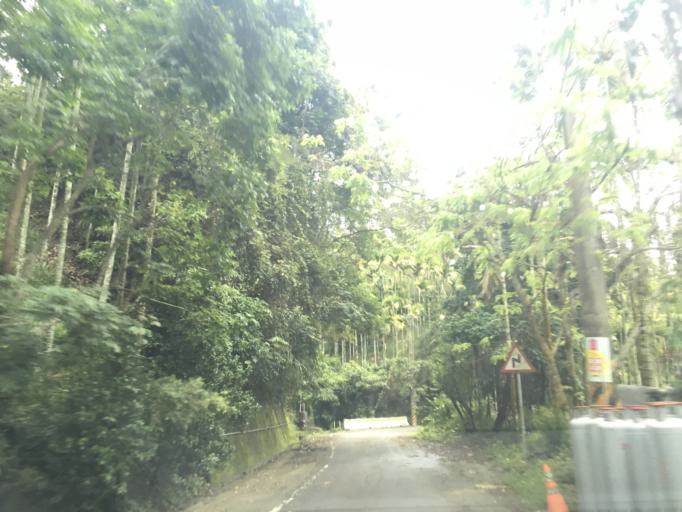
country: TW
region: Taiwan
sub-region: Yunlin
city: Douliu
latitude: 23.5654
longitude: 120.6276
